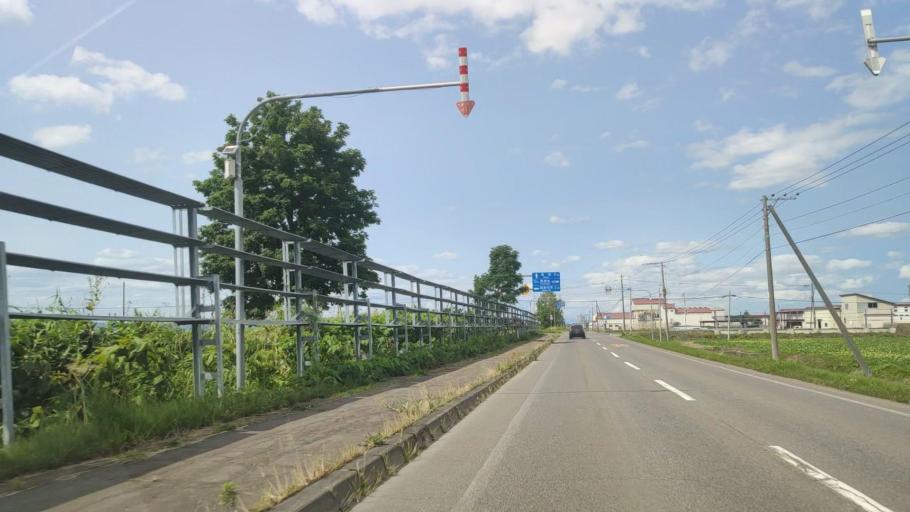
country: JP
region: Hokkaido
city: Nayoro
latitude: 44.1997
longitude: 142.4158
